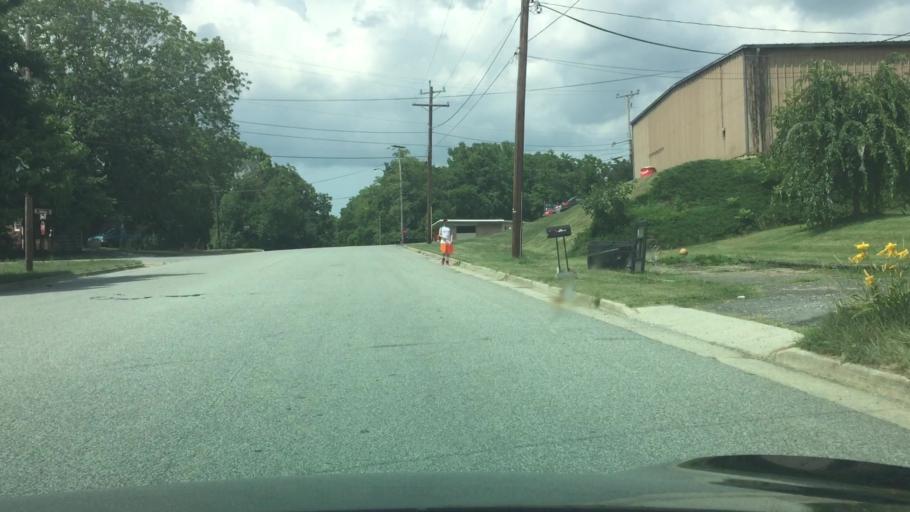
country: US
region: Virginia
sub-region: Wythe County
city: Wytheville
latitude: 36.9439
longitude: -81.0808
